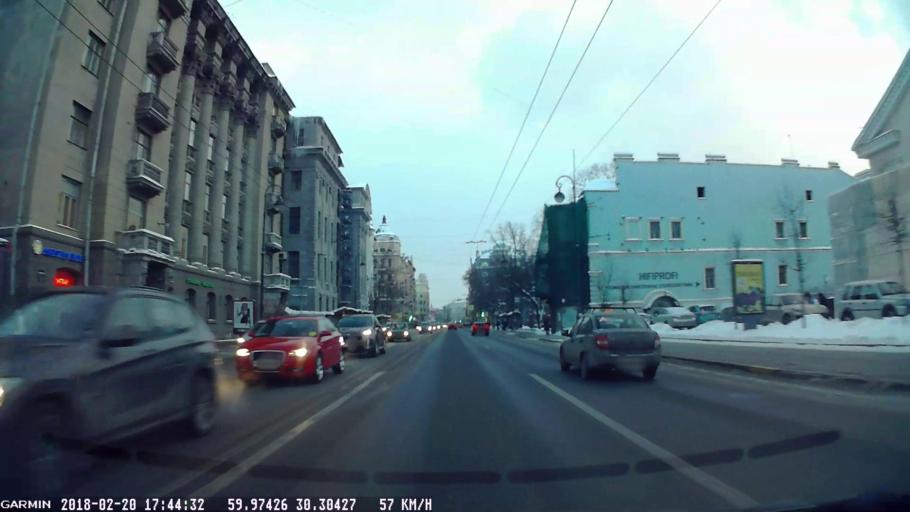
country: RU
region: St.-Petersburg
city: Petrogradka
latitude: 59.9737
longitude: 30.3047
